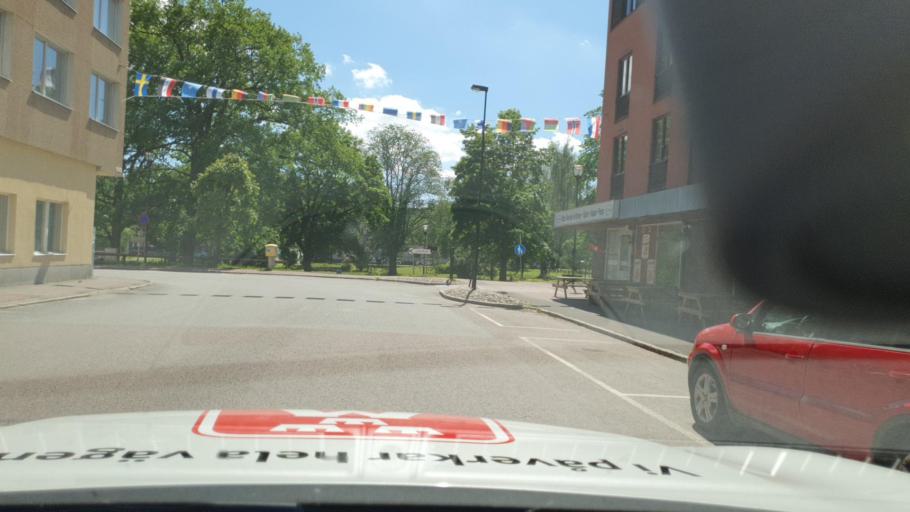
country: SE
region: Vaermland
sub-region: Filipstads Kommun
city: Filipstad
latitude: 59.7130
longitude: 14.1649
